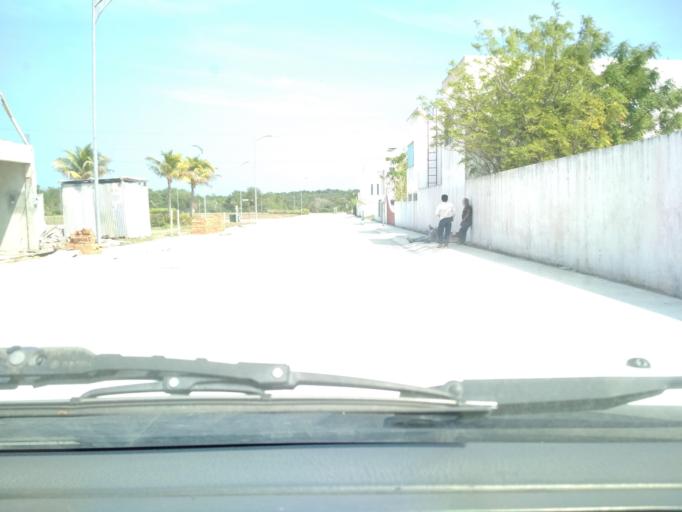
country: MX
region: Veracruz
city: Boca del Rio
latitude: 19.1056
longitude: -96.1221
